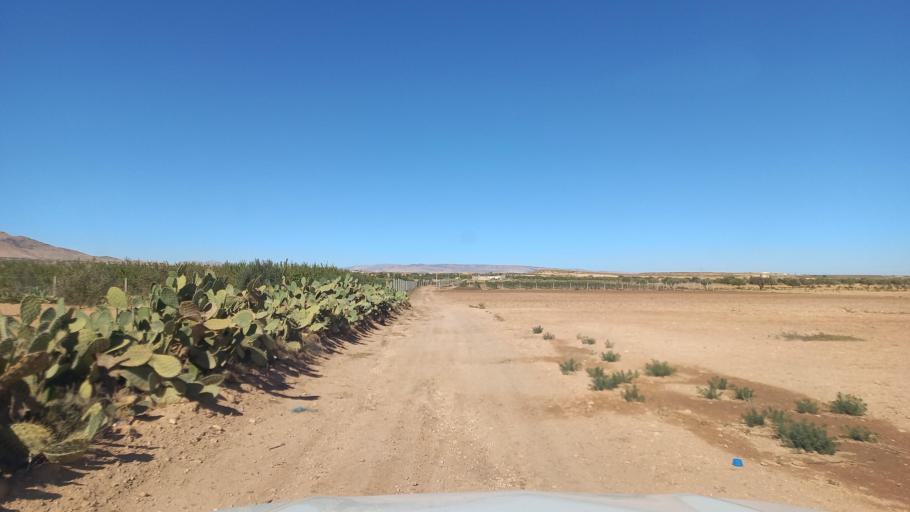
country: TN
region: Al Qasrayn
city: Sbiba
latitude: 35.3910
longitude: 9.0817
